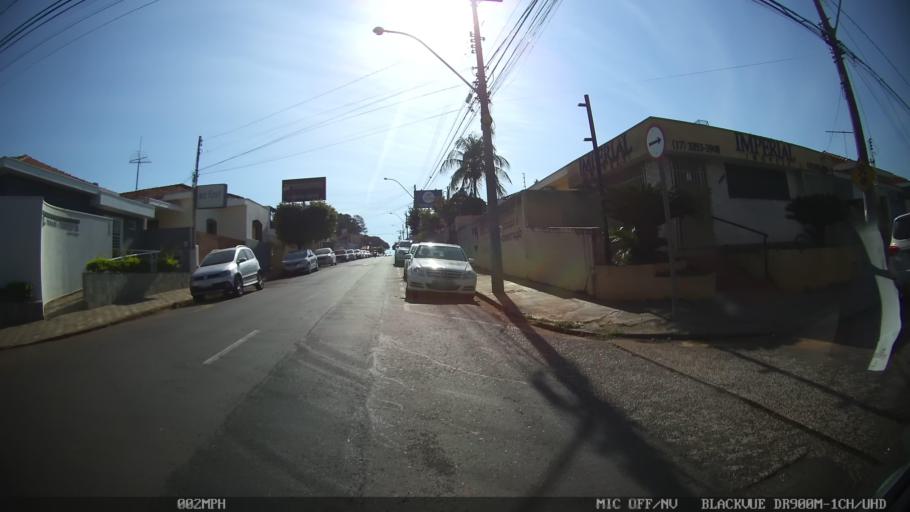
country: BR
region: Sao Paulo
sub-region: Sao Jose Do Rio Preto
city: Sao Jose do Rio Preto
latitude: -20.8062
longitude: -49.3887
